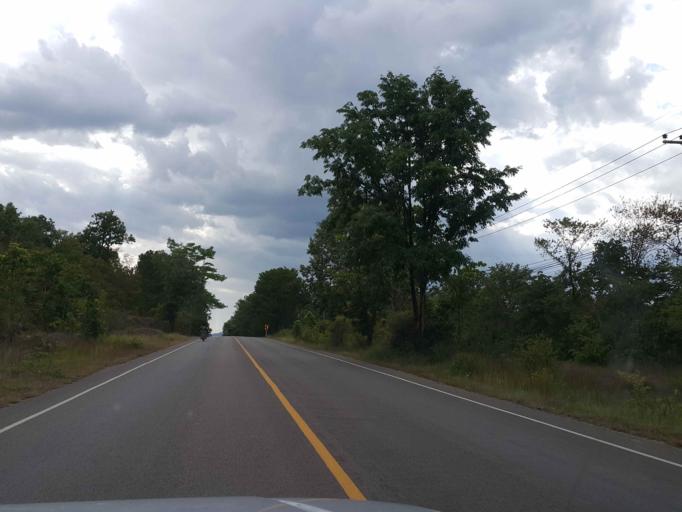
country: TH
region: Lampang
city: Thoen
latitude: 17.6491
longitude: 99.2740
